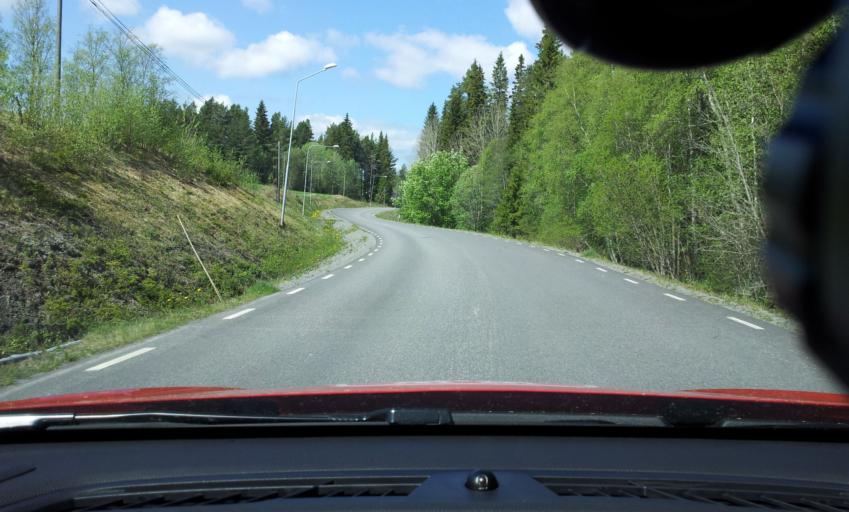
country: SE
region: Jaemtland
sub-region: OEstersunds Kommun
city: Ostersund
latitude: 62.9916
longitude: 14.5909
